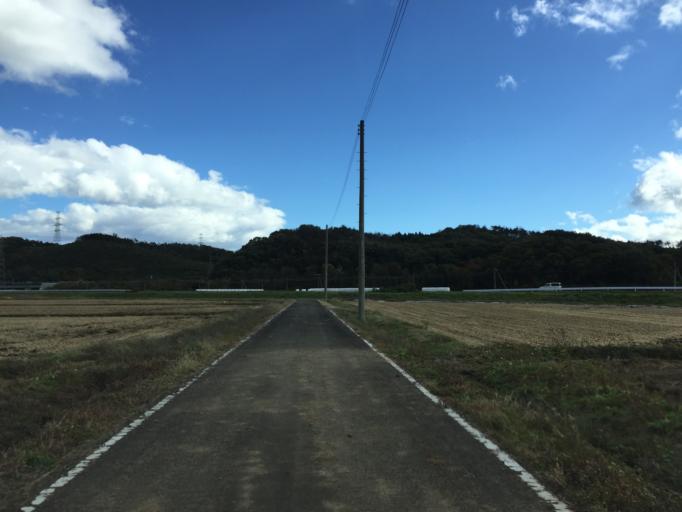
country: JP
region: Fukushima
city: Nihommatsu
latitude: 37.6585
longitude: 140.4310
